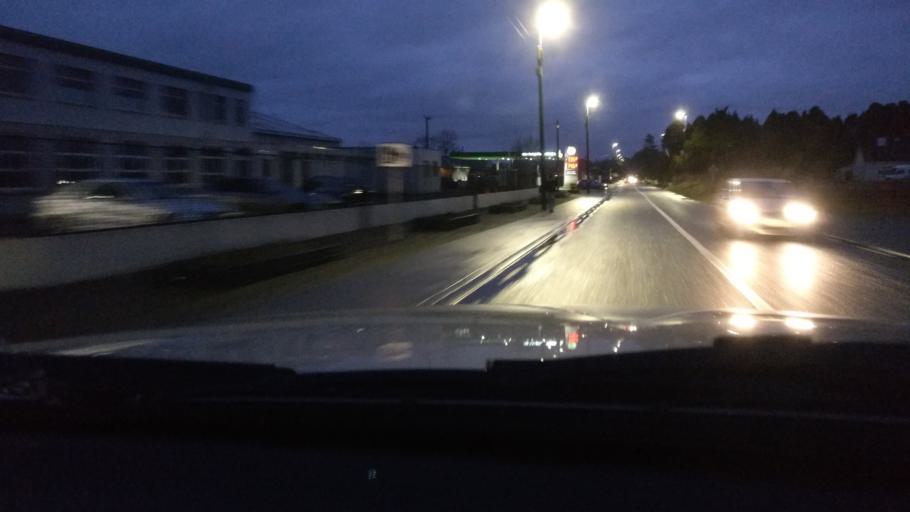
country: IE
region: Leinster
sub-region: An Longfort
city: Ballymahon
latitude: 53.5668
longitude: -7.7619
